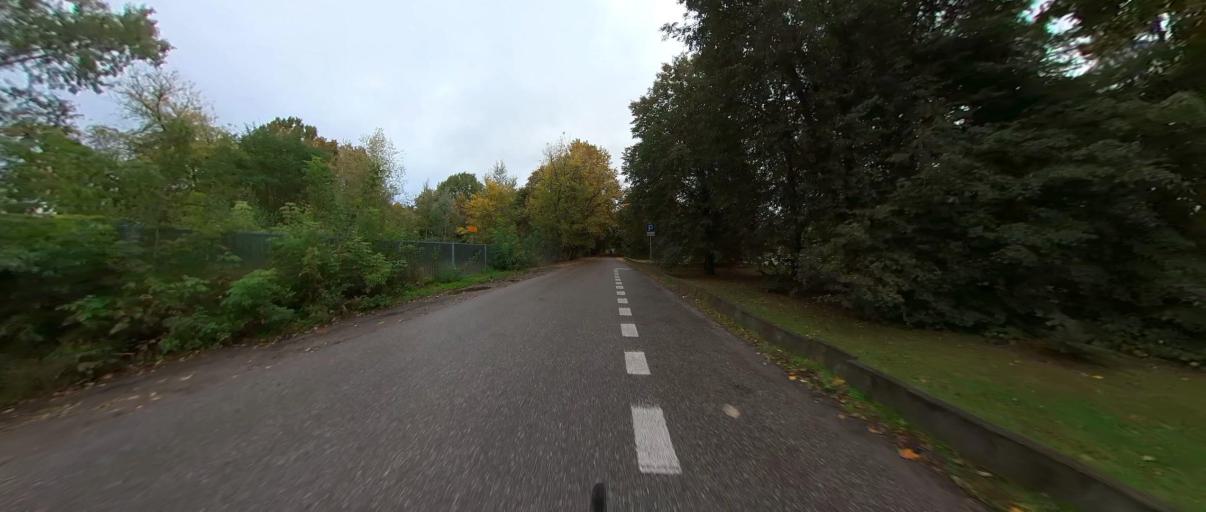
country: PL
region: Masovian Voivodeship
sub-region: Warszawa
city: Ochota
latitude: 52.2118
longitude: 20.9940
